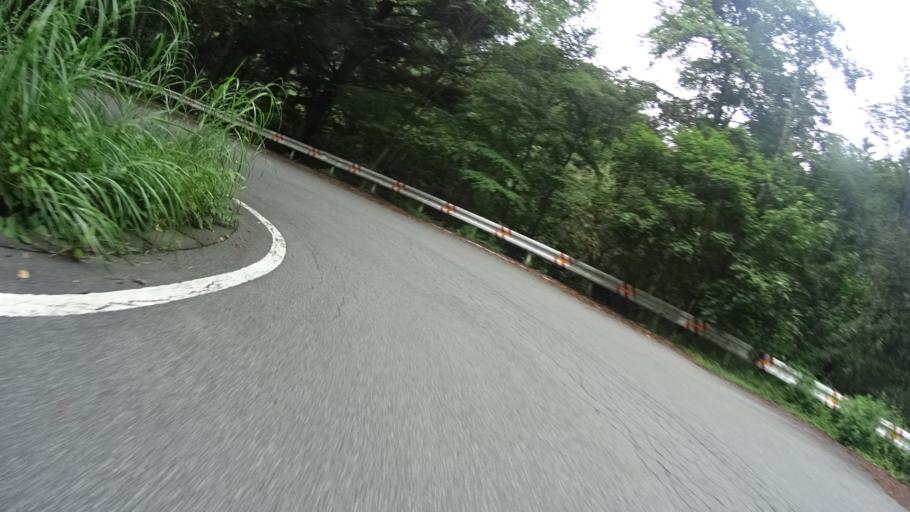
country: JP
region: Yamanashi
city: Enzan
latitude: 35.7918
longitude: 138.6830
